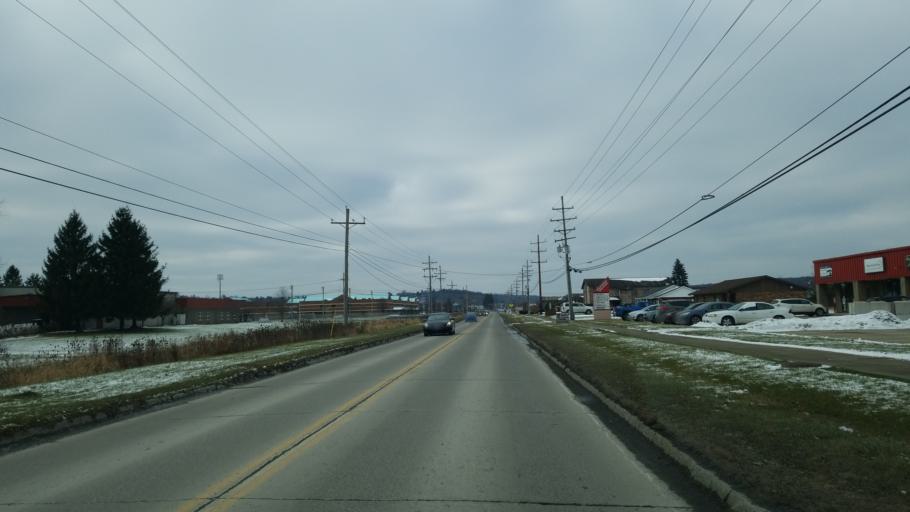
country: US
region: Pennsylvania
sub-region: Clearfield County
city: DuBois
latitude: 41.1230
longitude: -78.7499
